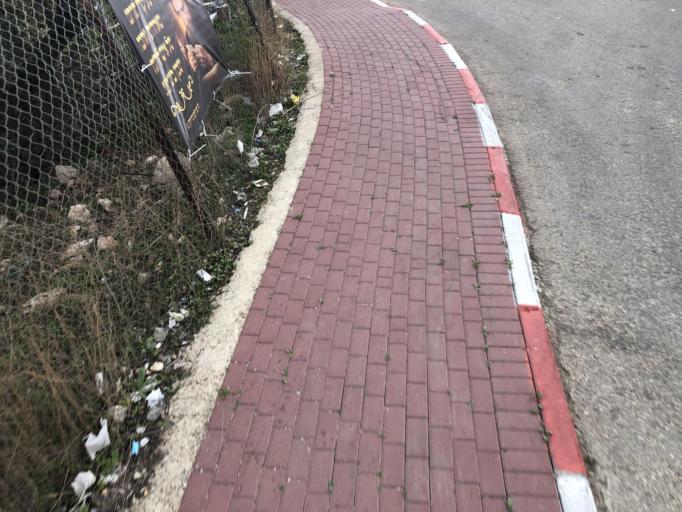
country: PS
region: West Bank
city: Dayr Qiddis
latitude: 31.9421
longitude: 35.0460
